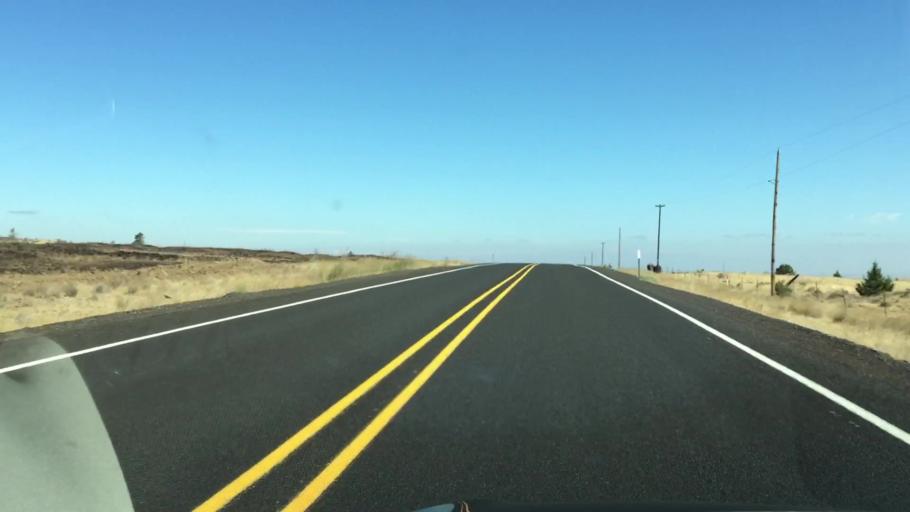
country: US
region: Oregon
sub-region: Jefferson County
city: Warm Springs
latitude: 44.9929
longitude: -120.9951
